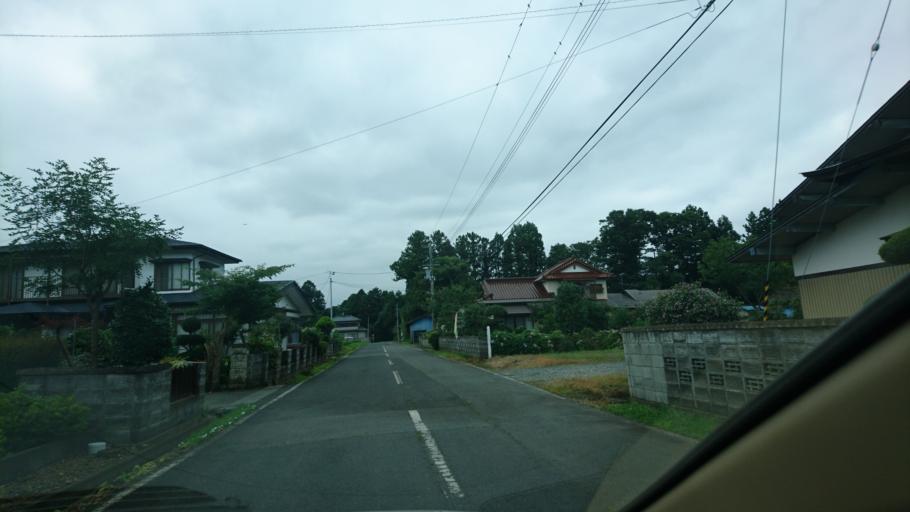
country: JP
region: Iwate
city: Kitakami
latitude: 39.2279
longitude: 141.1007
